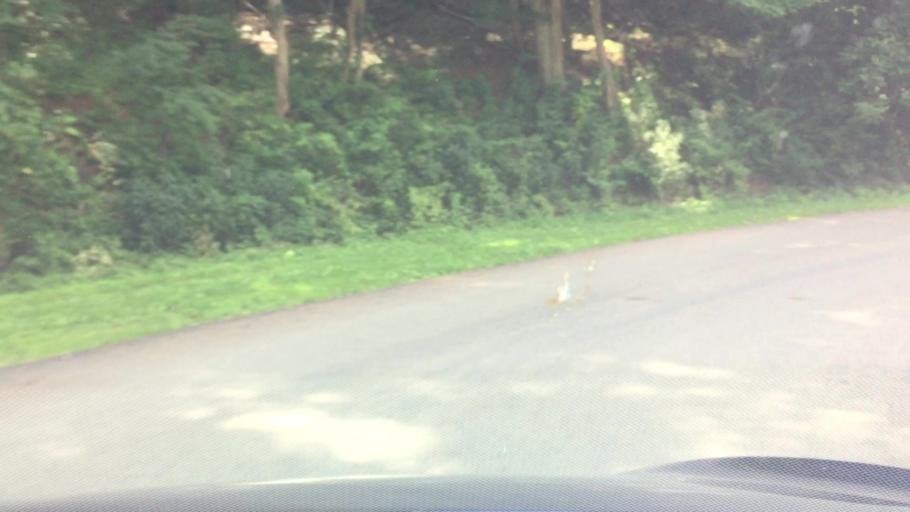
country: US
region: Virginia
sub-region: Wythe County
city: Wytheville
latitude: 36.9276
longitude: -81.0651
